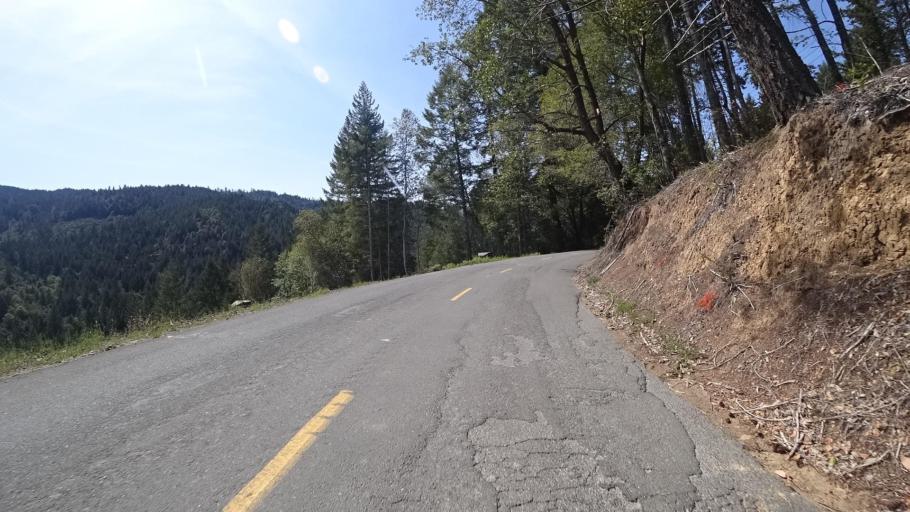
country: US
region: California
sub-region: Humboldt County
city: Redway
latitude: 40.3684
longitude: -123.7346
